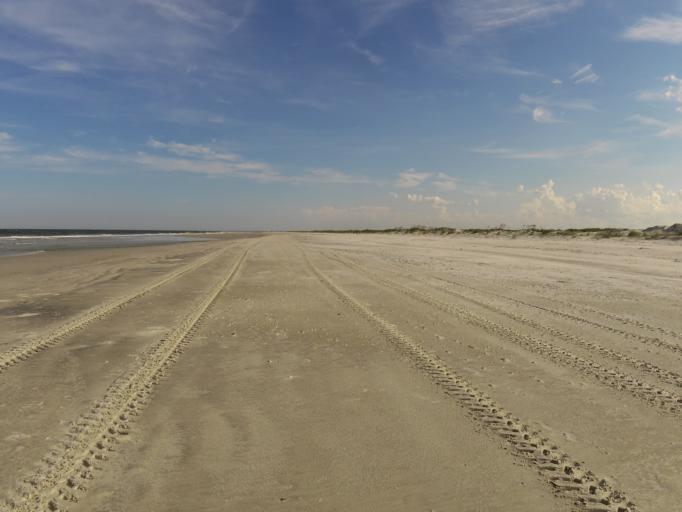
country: US
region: Florida
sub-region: Duval County
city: Atlantic Beach
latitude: 30.4460
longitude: -81.4093
